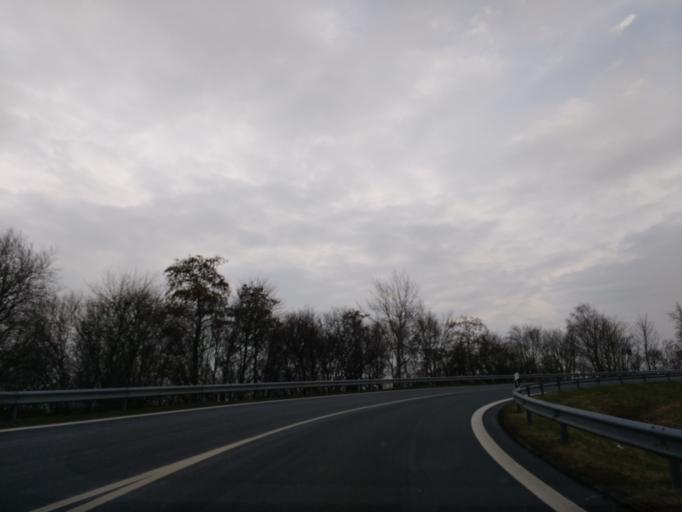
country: DE
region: Lower Saxony
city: Cuxhaven
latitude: 53.8192
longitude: 8.7120
